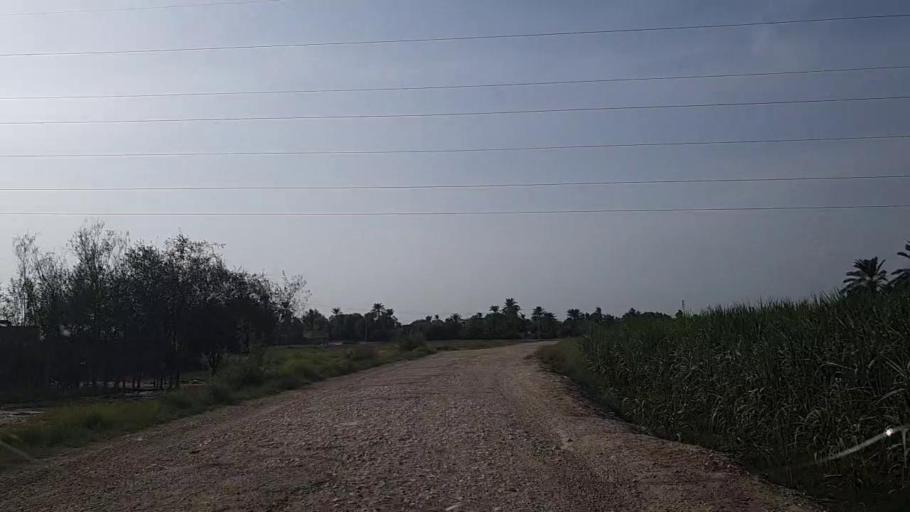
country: PK
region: Sindh
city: Ghotki
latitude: 28.0074
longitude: 69.2962
